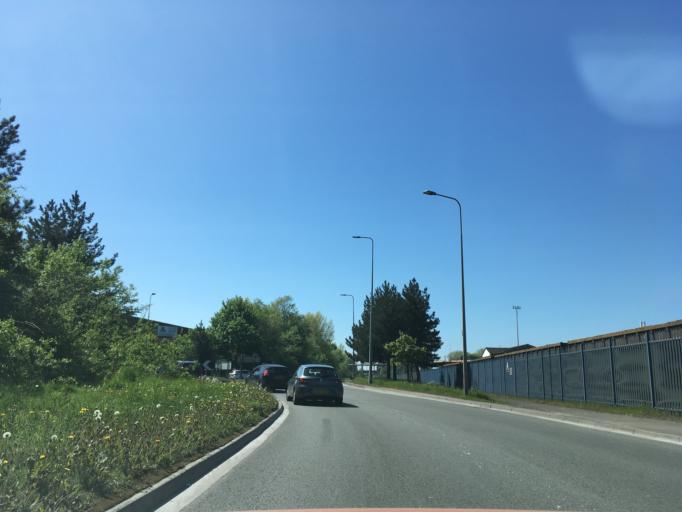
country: GB
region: Wales
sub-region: Cardiff
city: Cardiff
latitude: 51.4764
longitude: -3.1389
